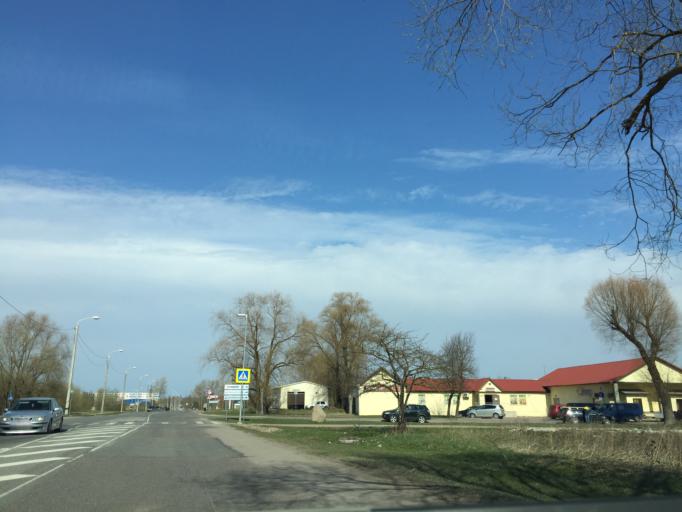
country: EE
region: Ida-Virumaa
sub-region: Narva linn
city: Narva
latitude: 59.3873
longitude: 28.1886
